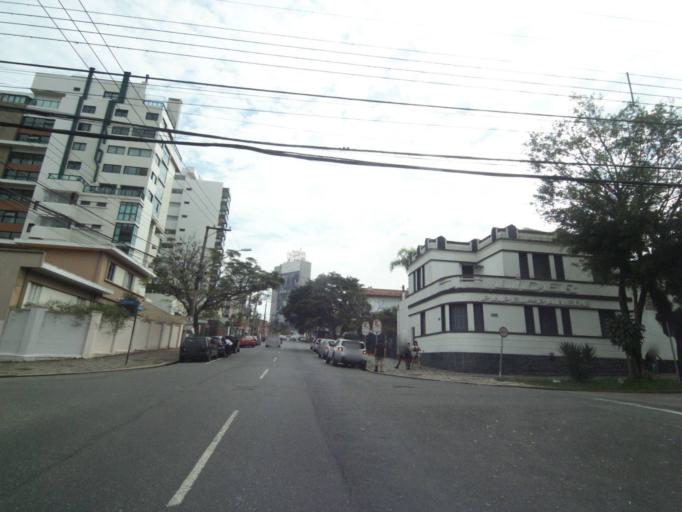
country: BR
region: Parana
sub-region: Curitiba
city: Curitiba
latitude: -25.4276
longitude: -49.2789
